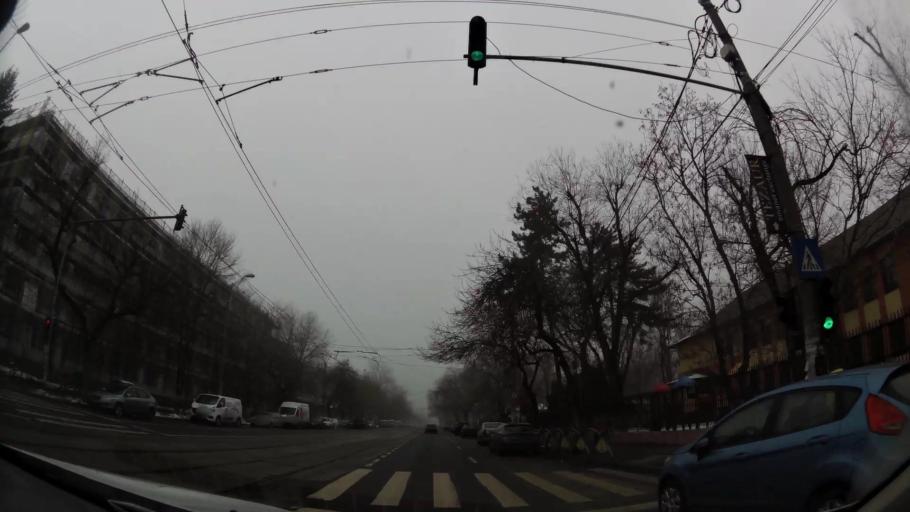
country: RO
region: Ilfov
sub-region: Comuna Chiajna
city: Rosu
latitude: 44.4613
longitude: 26.0455
